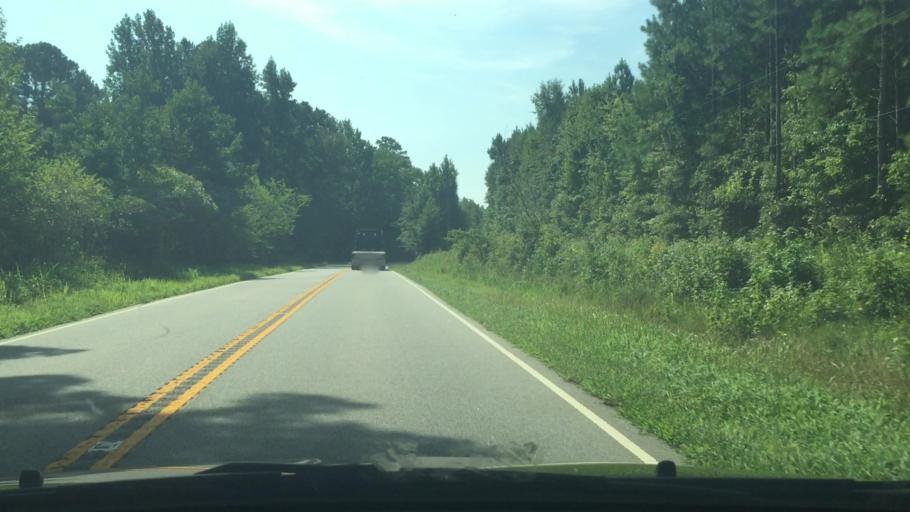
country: US
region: Virginia
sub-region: Sussex County
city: Sussex
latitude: 36.8702
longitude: -77.1434
